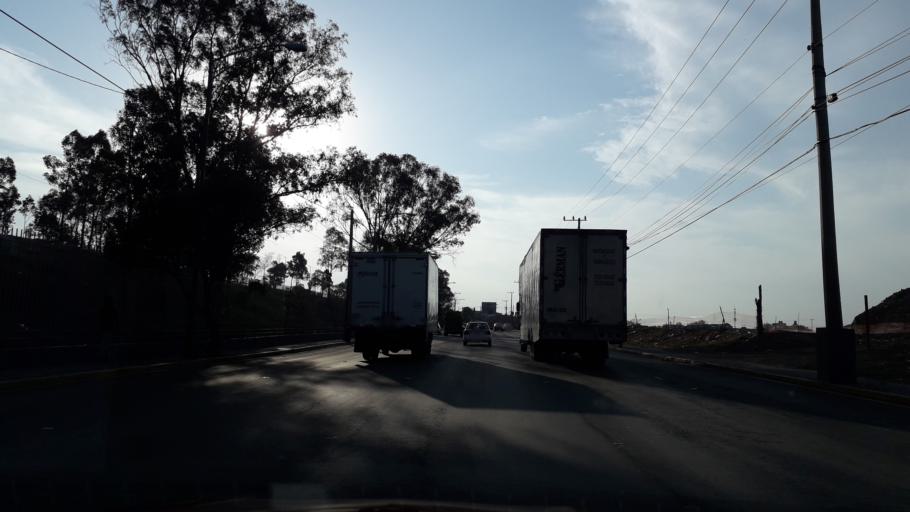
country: MX
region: Mexico City
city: Iztapalapa
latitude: 19.3681
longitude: -99.0440
